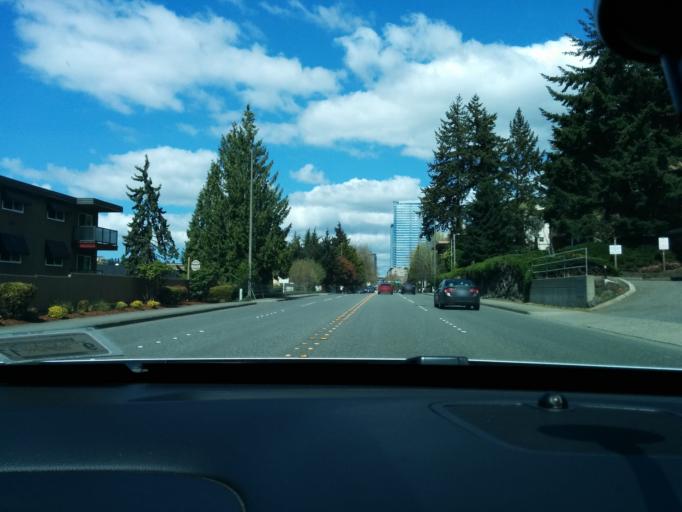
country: US
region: Washington
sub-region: King County
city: Bellevue
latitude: 47.6053
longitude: -122.2014
